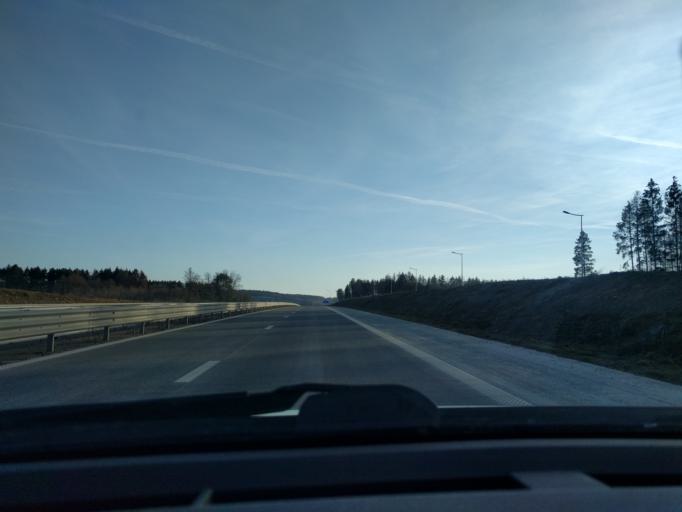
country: BE
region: Wallonia
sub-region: Province de Namur
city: Couvin
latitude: 50.0629
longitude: 4.5050
